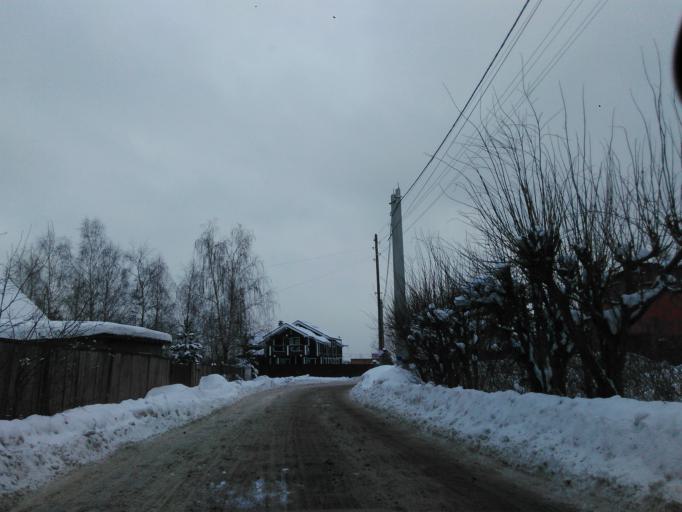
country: RU
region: Moskovskaya
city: Yakhroma
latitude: 56.2691
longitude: 37.4534
